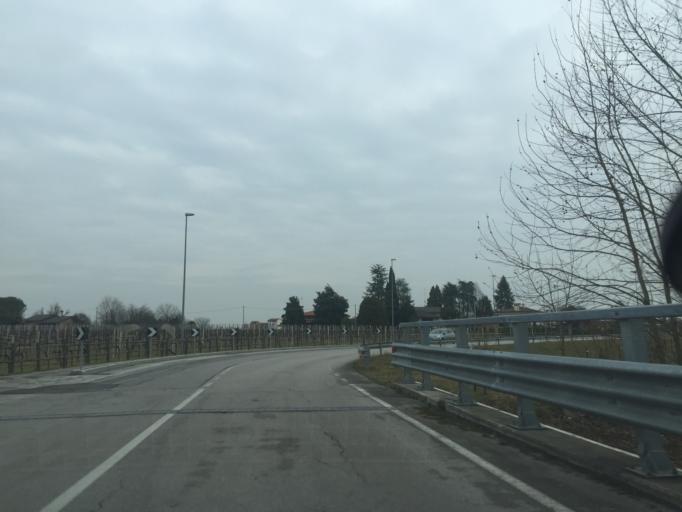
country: IT
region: Friuli Venezia Giulia
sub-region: Provincia di Pordenone
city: Cavolano-Schiavoi
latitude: 45.9383
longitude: 12.5185
